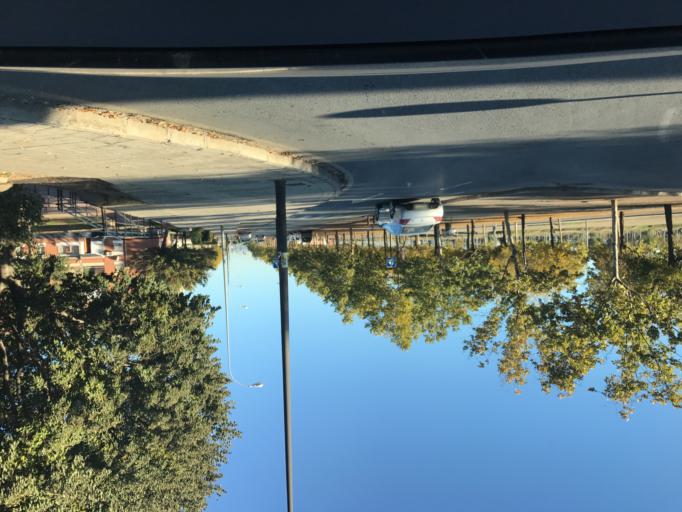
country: ES
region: Andalusia
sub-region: Provincia de Granada
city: Pulianas
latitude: 37.2096
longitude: -3.6136
